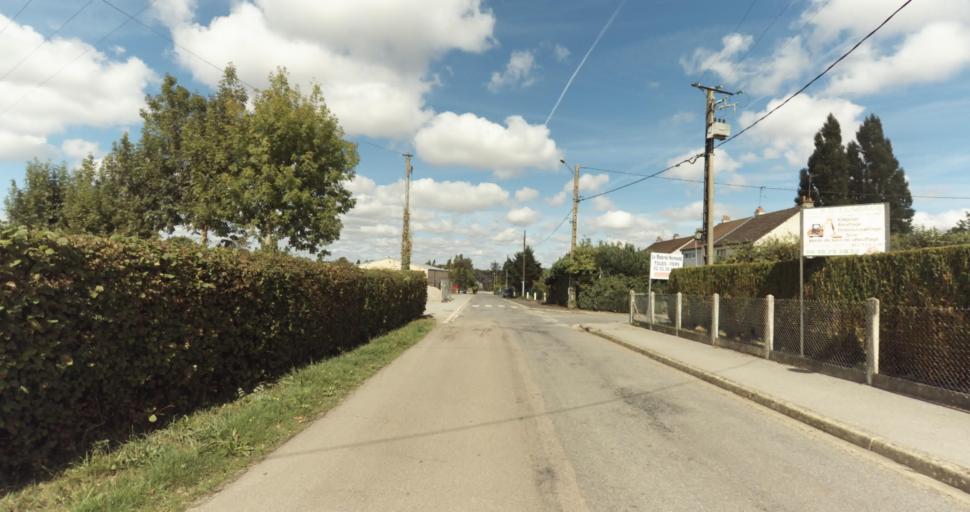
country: FR
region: Lower Normandy
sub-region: Departement de l'Orne
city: Gace
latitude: 48.8905
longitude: 0.3395
